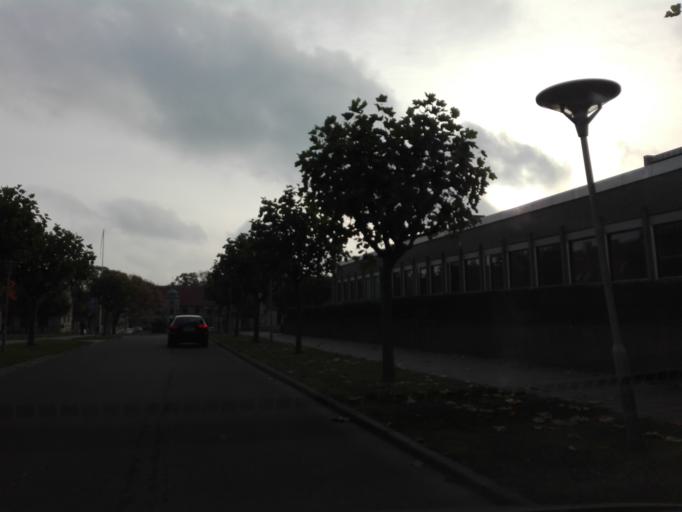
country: DK
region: Central Jutland
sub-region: Arhus Kommune
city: Arhus
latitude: 56.1863
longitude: 10.2288
